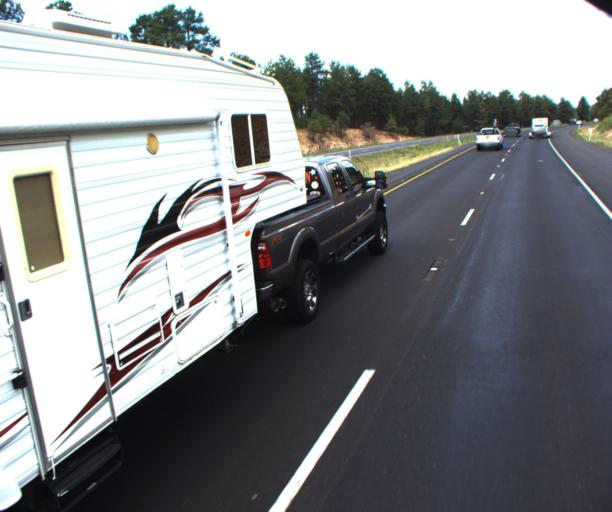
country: US
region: Arizona
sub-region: Coconino County
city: Kachina Village
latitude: 35.1270
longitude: -111.6831
